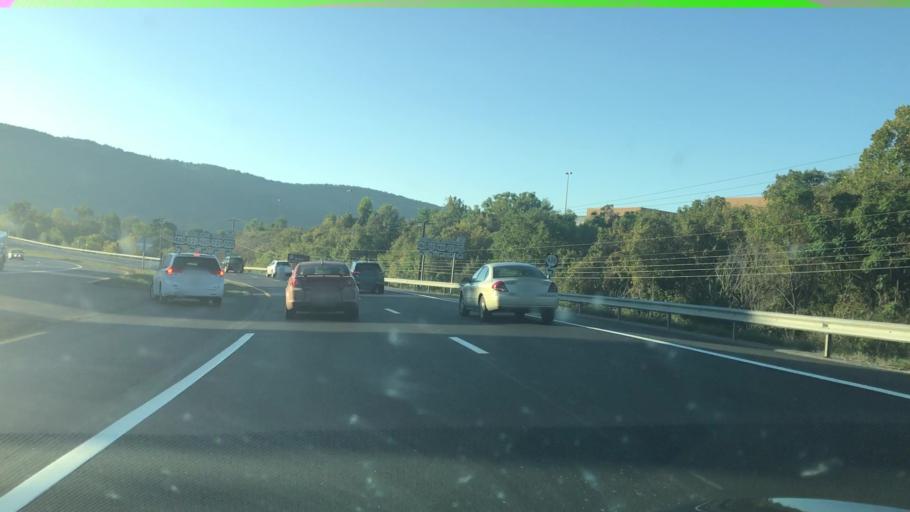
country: US
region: Virginia
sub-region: Botetourt County
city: Laymantown
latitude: 37.3280
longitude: -79.8725
